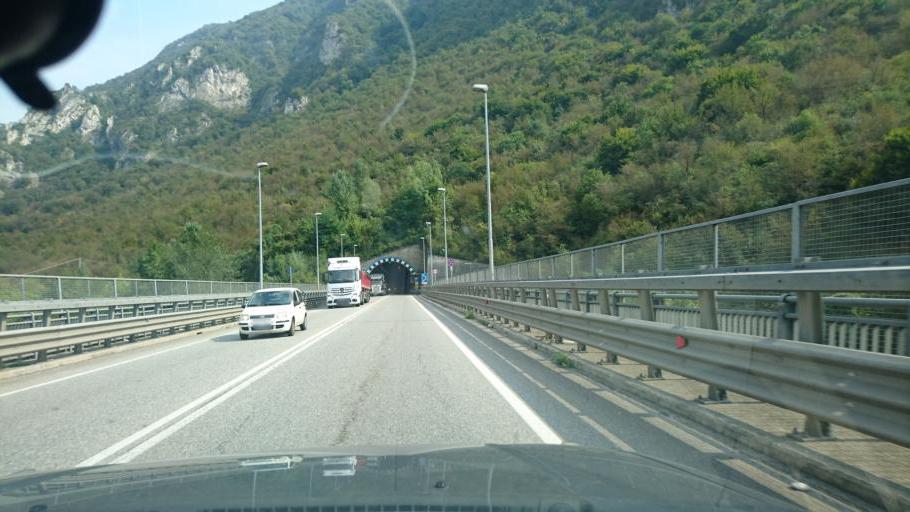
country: IT
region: Lombardy
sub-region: Provincia di Brescia
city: Vobarno
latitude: 45.6432
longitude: 10.4652
